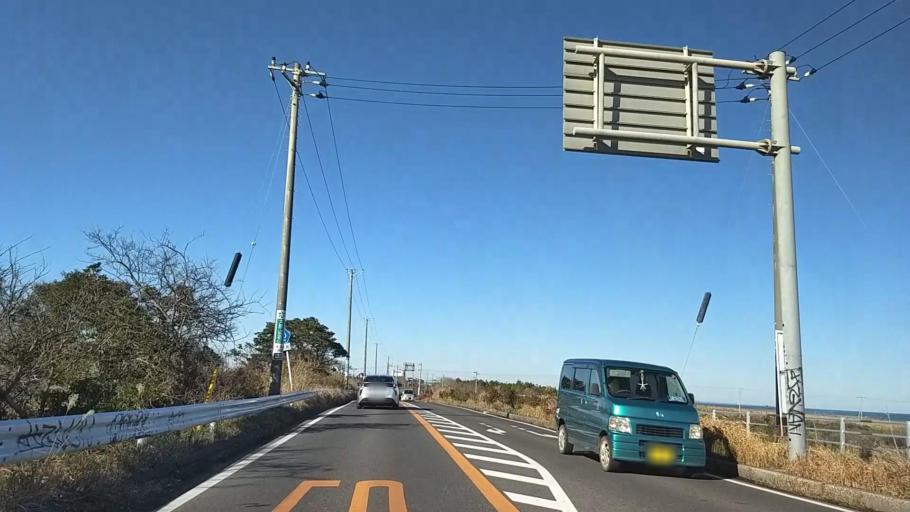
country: JP
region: Chiba
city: Ohara
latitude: 35.3334
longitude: 140.3925
